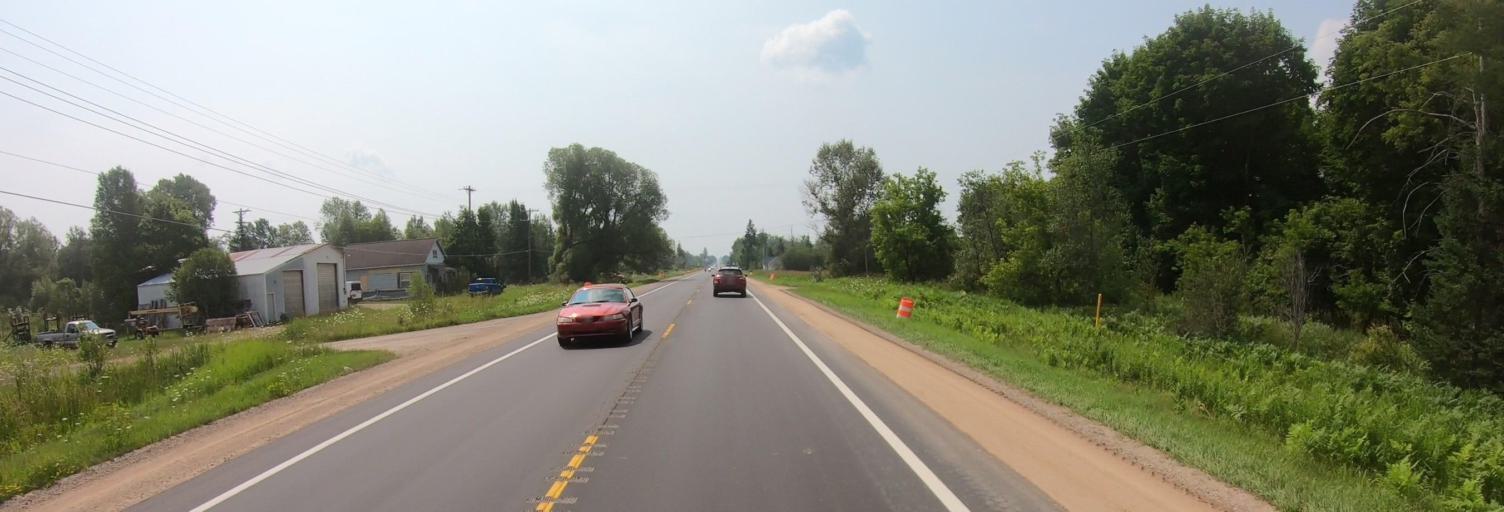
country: US
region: Michigan
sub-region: Luce County
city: Newberry
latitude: 46.3665
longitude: -85.5099
